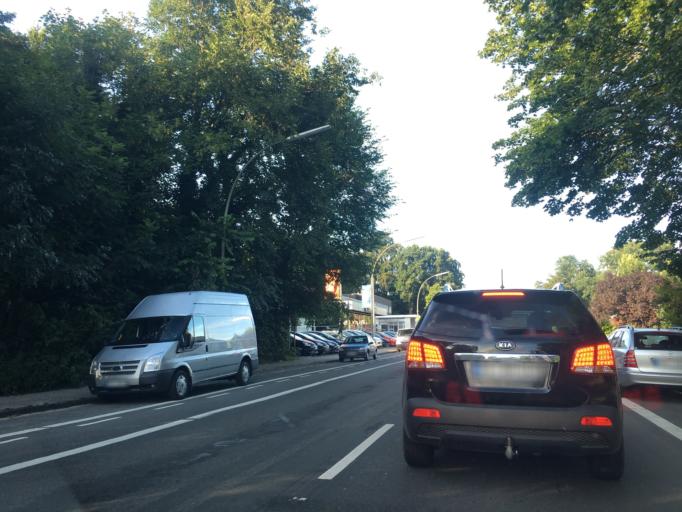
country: DE
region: North Rhine-Westphalia
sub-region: Regierungsbezirk Munster
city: Dulmen
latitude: 51.8258
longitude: 7.2739
